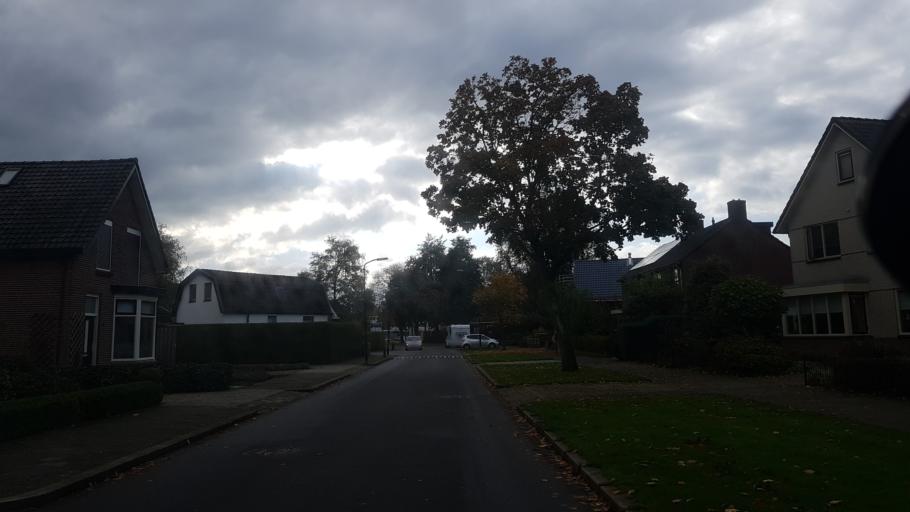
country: NL
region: Gelderland
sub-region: Gemeente Apeldoorn
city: Apeldoorn
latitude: 52.2321
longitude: 5.9617
